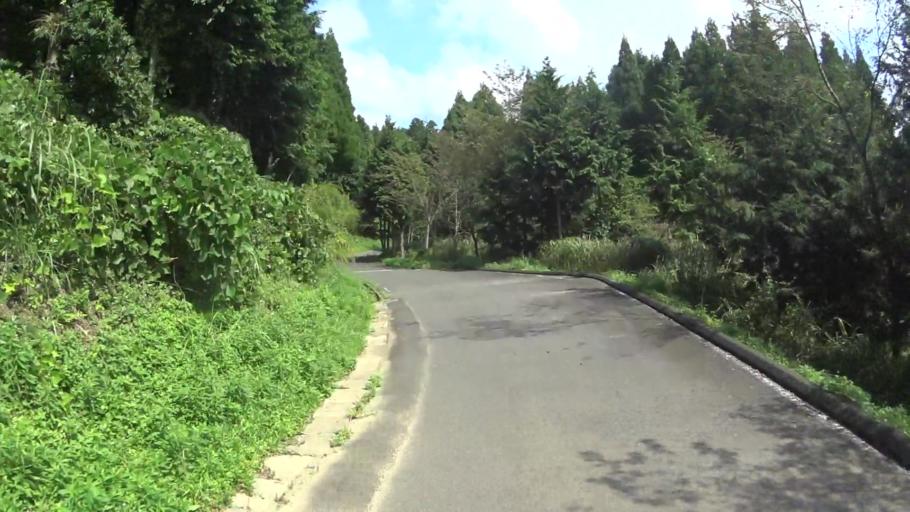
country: JP
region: Kyoto
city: Miyazu
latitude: 35.6648
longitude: 135.2315
